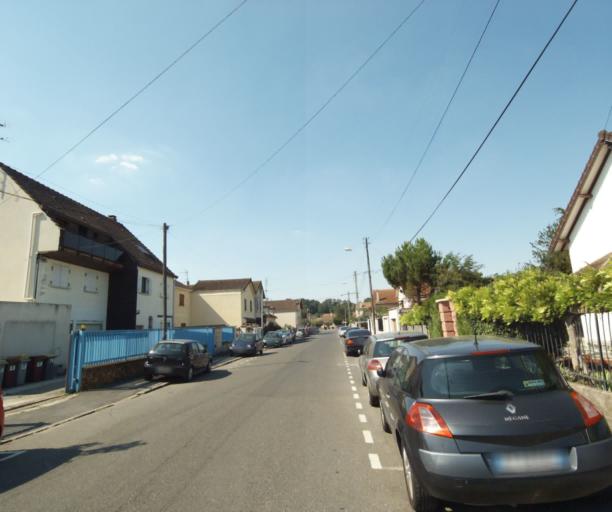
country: FR
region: Ile-de-France
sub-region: Departement de Seine-et-Marne
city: Pomponne
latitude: 48.8773
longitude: 2.6922
